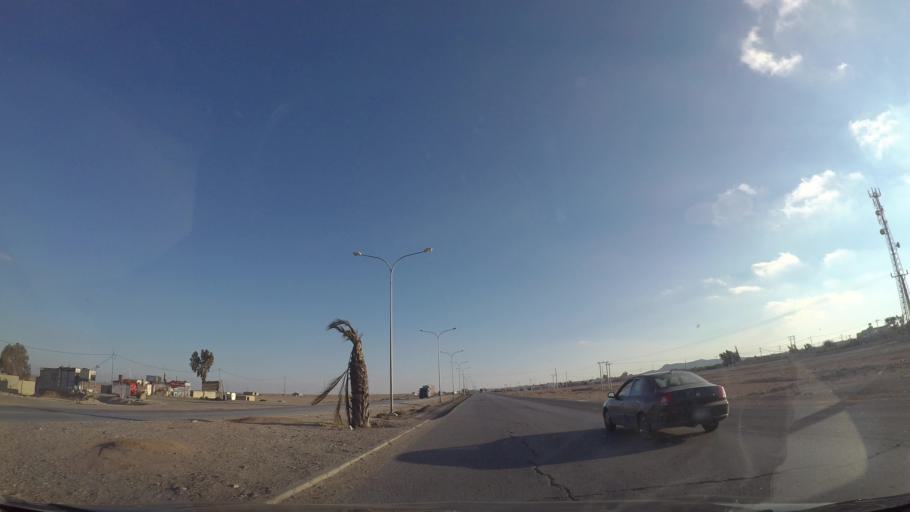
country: JO
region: Tafielah
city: Busayra
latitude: 30.5252
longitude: 35.7995
